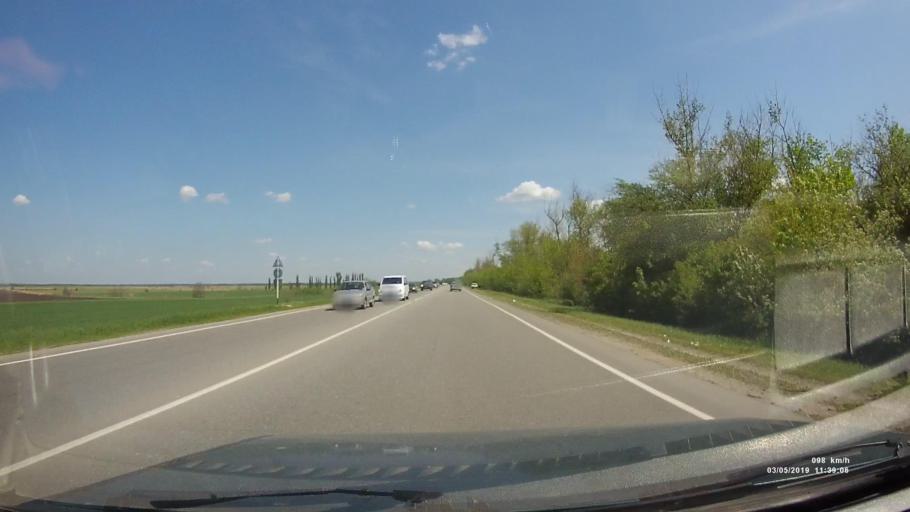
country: RU
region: Rostov
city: Ol'ginskaya
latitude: 47.1321
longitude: 39.9795
